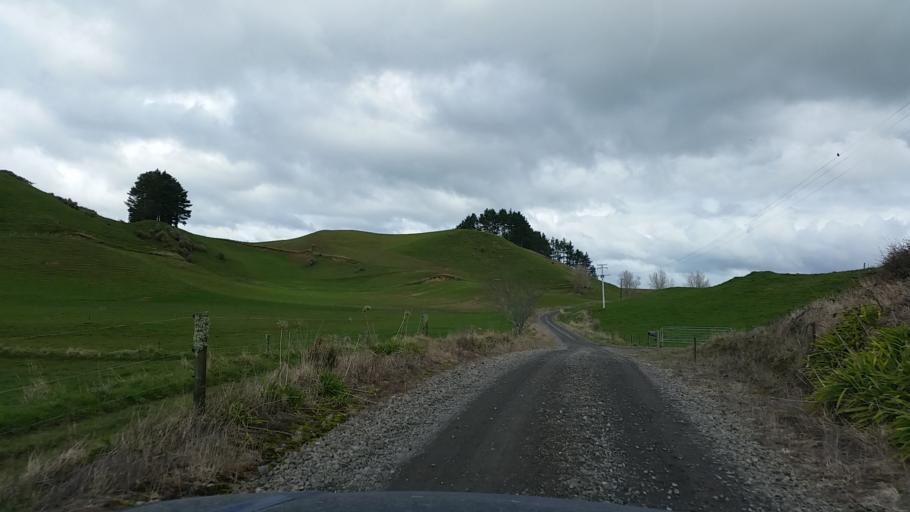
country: NZ
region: Taranaki
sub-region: South Taranaki District
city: Eltham
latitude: -39.3524
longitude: 174.3842
